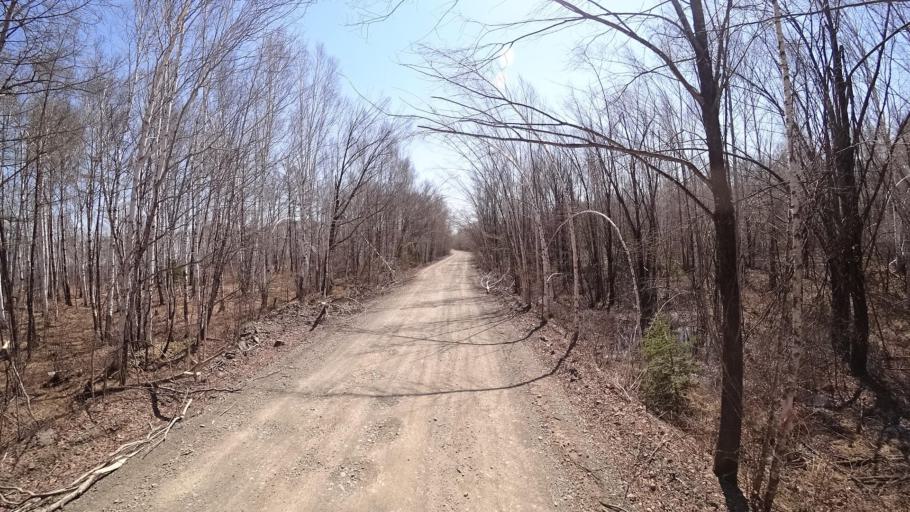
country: RU
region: Khabarovsk Krai
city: Khurba
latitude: 50.4171
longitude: 136.8371
